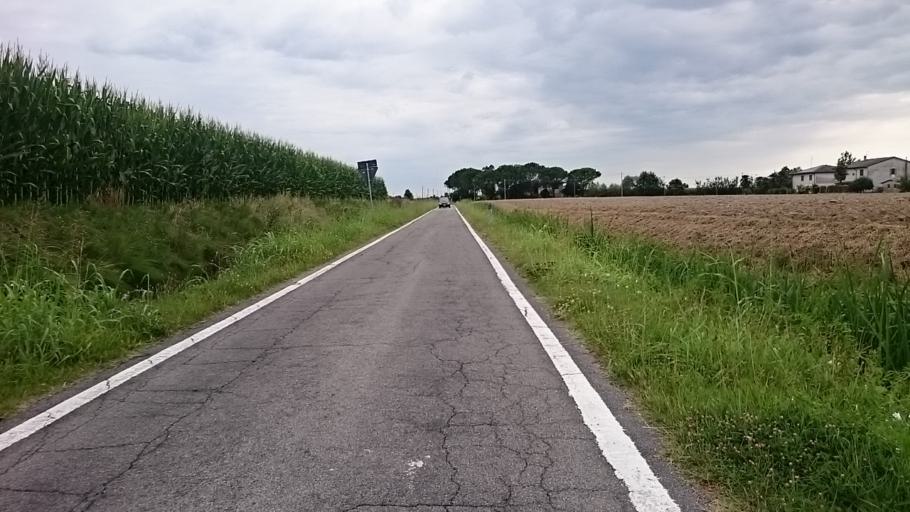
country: IT
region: Veneto
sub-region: Provincia di Padova
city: Masera di Padova
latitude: 45.3327
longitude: 11.8756
